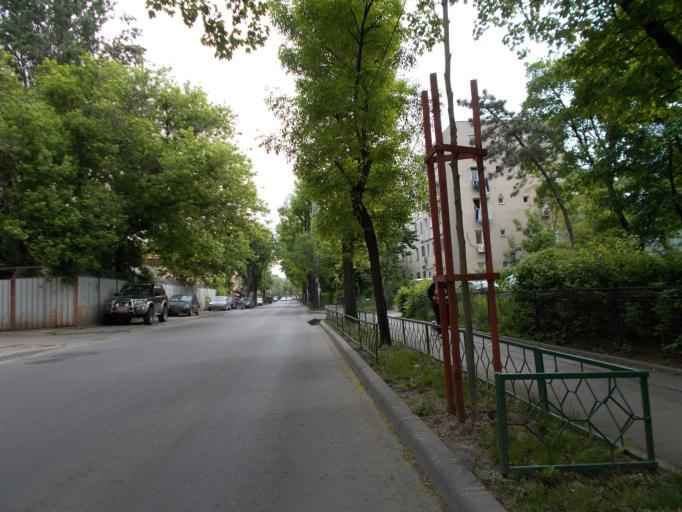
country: RO
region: Bucuresti
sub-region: Municipiul Bucuresti
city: Bucuresti
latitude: 44.3868
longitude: 26.0947
